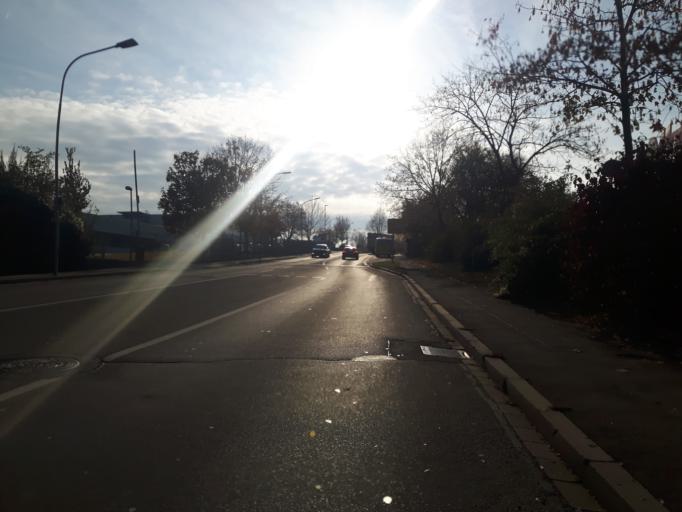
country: DE
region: Rheinland-Pfalz
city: Alzey
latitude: 49.7466
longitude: 8.1391
